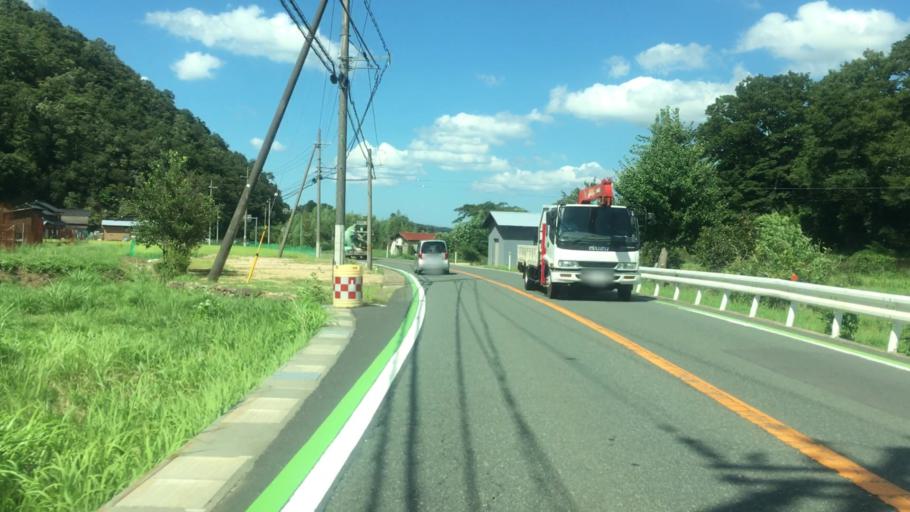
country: JP
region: Kyoto
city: Miyazu
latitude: 35.5833
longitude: 135.0353
